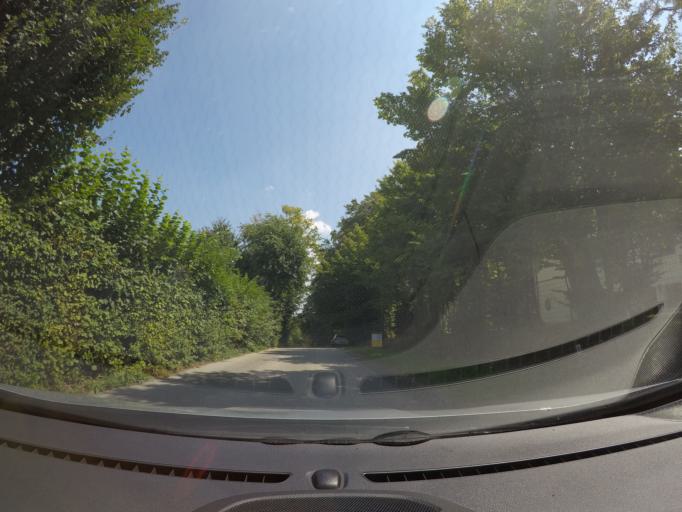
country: AT
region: Lower Austria
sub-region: Politischer Bezirk Wien-Umgebung
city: Mauerbach
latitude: 48.2702
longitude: 16.1596
